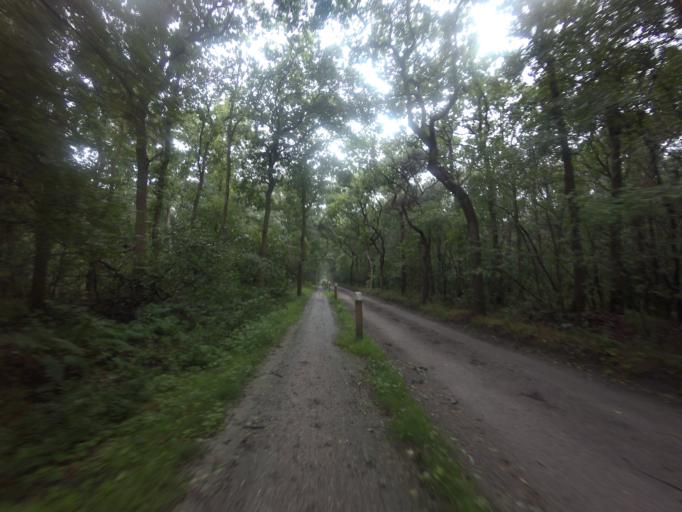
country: NL
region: Friesland
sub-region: Gemeente Heerenveen
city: Nieuwehorne
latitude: 52.9534
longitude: 6.0994
